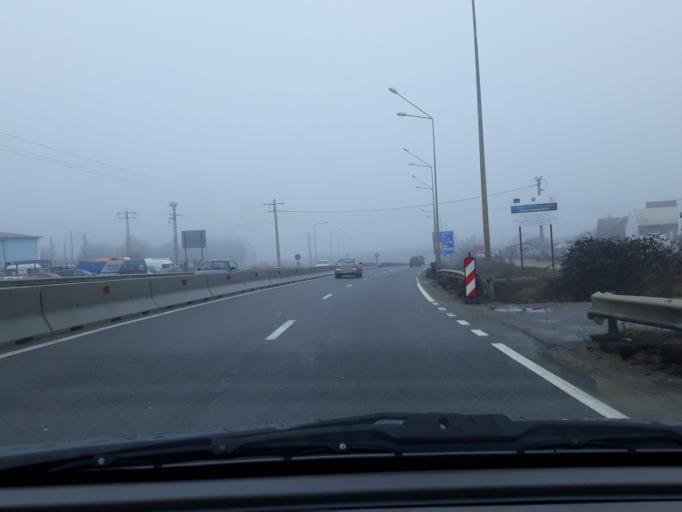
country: RO
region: Bihor
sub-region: Comuna Sanmartin
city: Sanmartin
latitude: 47.0250
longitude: 21.9461
